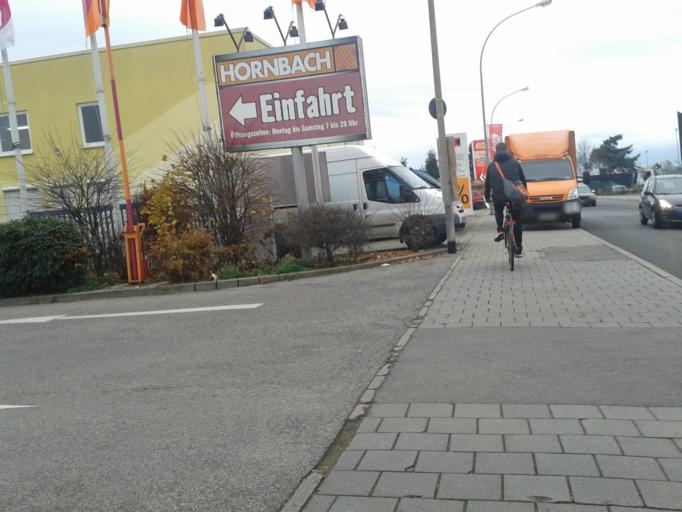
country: DE
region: Bavaria
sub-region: Upper Franconia
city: Hallstadt
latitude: 49.9086
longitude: 10.8786
